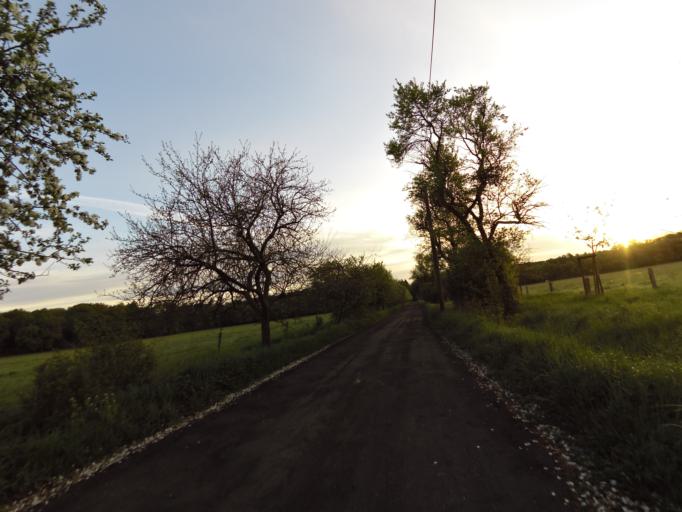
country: DE
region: North Rhine-Westphalia
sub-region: Regierungsbezirk Koln
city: Wachtberg
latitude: 50.6839
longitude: 7.1071
